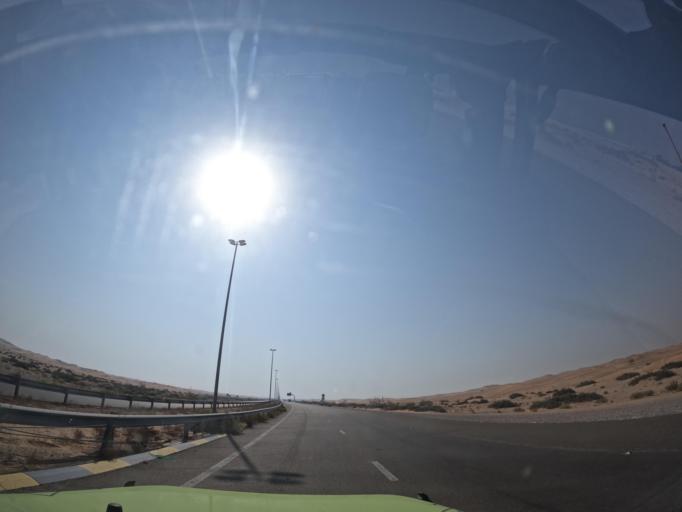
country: OM
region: Al Buraimi
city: Al Buraymi
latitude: 24.5180
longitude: 55.5564
